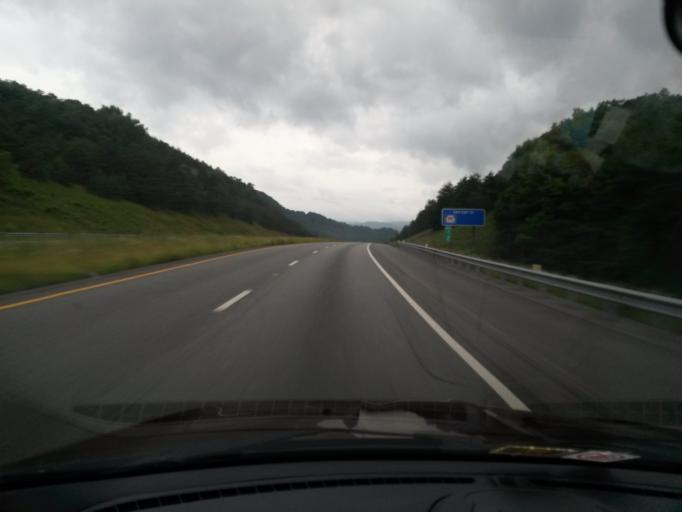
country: US
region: Virginia
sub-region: City of Covington
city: Covington
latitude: 37.7920
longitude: -80.0389
